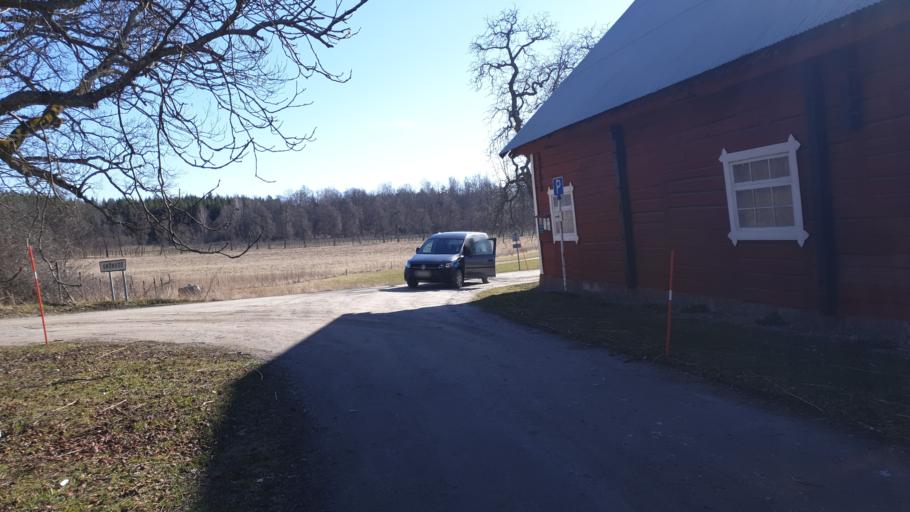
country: SE
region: Uppsala
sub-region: Enkopings Kommun
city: Dalby
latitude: 59.4753
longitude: 17.2503
